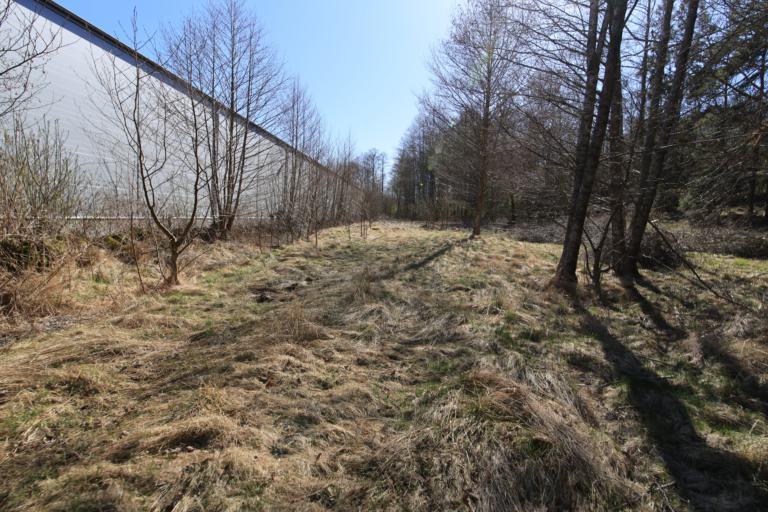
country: SE
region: Halland
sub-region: Varbergs Kommun
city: Varberg
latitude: 57.1665
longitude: 12.2727
